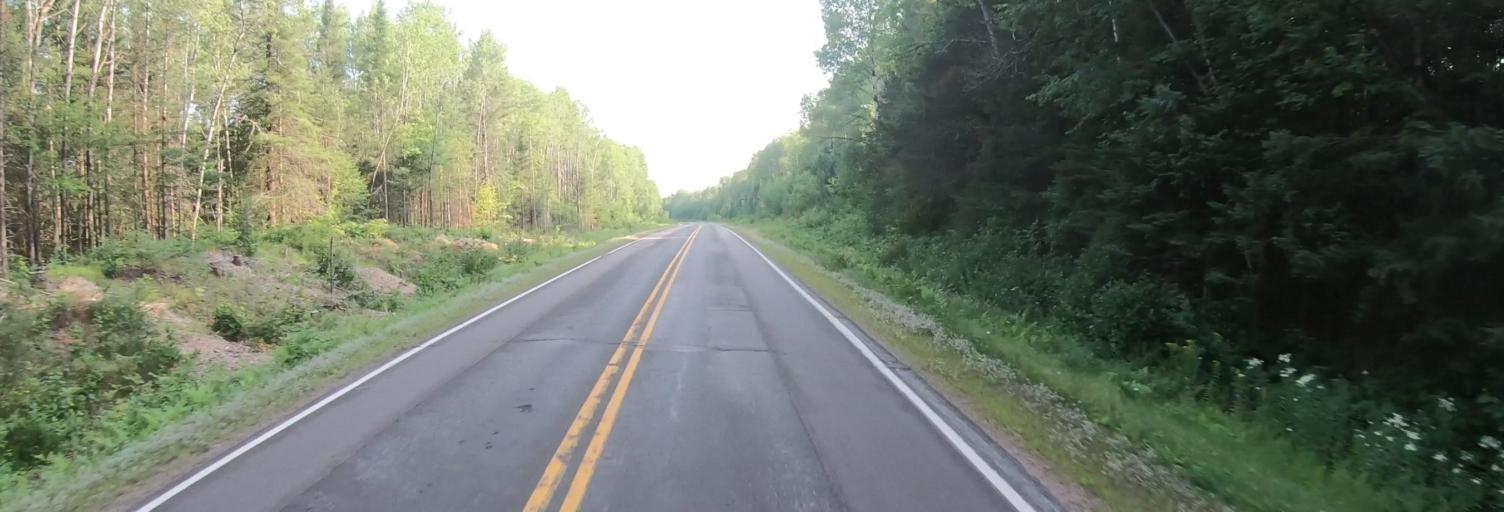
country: US
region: Wisconsin
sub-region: Ashland County
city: Ashland
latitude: 46.2681
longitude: -90.8406
